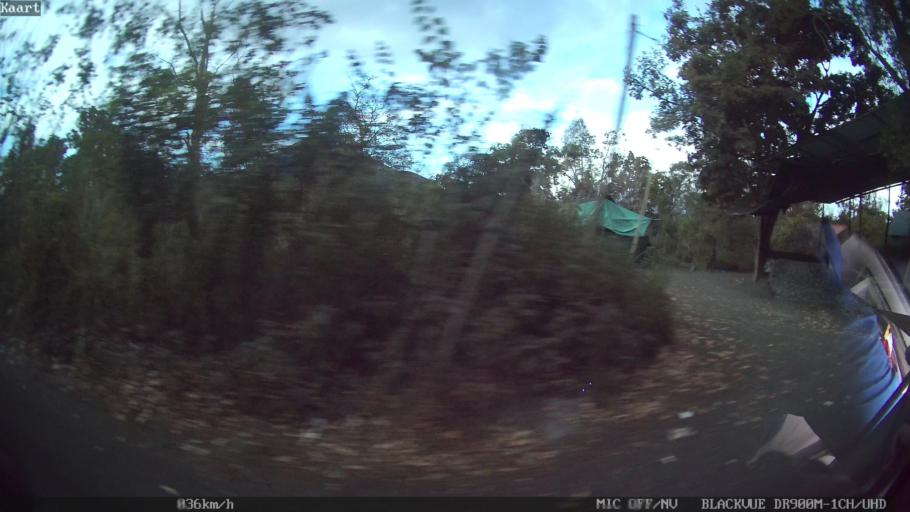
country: ID
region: Bali
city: Banjar Kedisan
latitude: -8.2531
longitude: 115.3492
